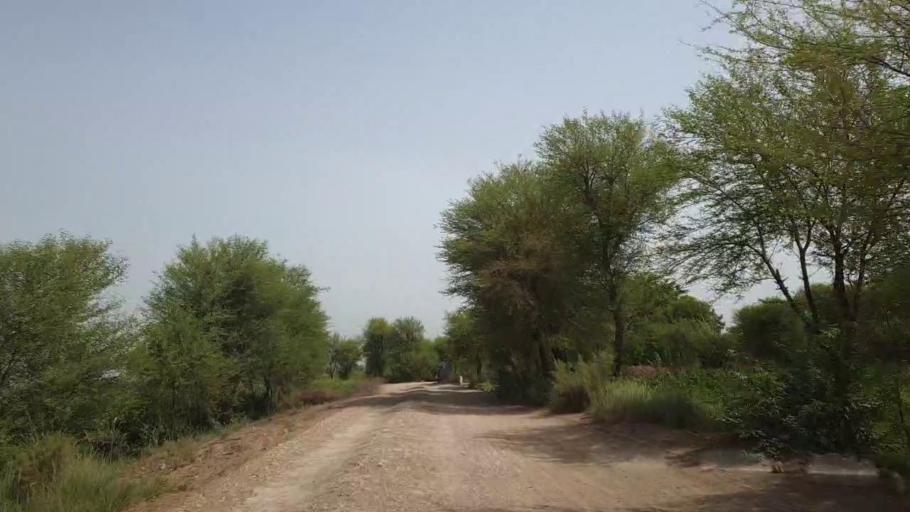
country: PK
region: Sindh
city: Sakrand
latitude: 26.1164
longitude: 68.3692
